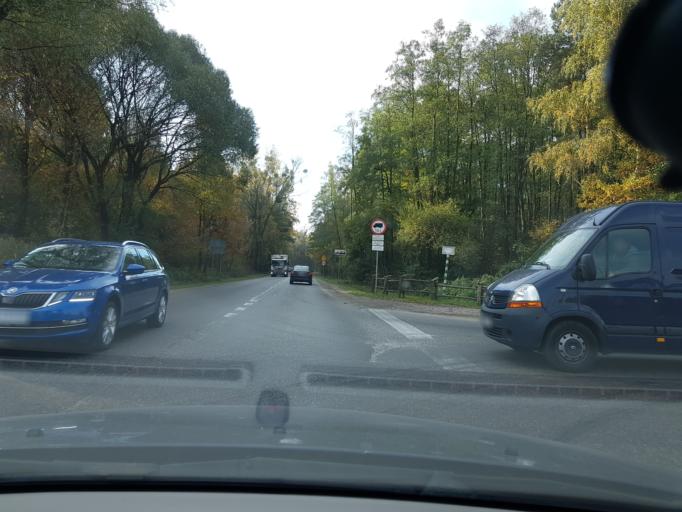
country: PL
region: Masovian Voivodeship
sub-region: Powiat warszawski zachodni
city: Babice
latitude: 52.2751
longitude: 20.8753
